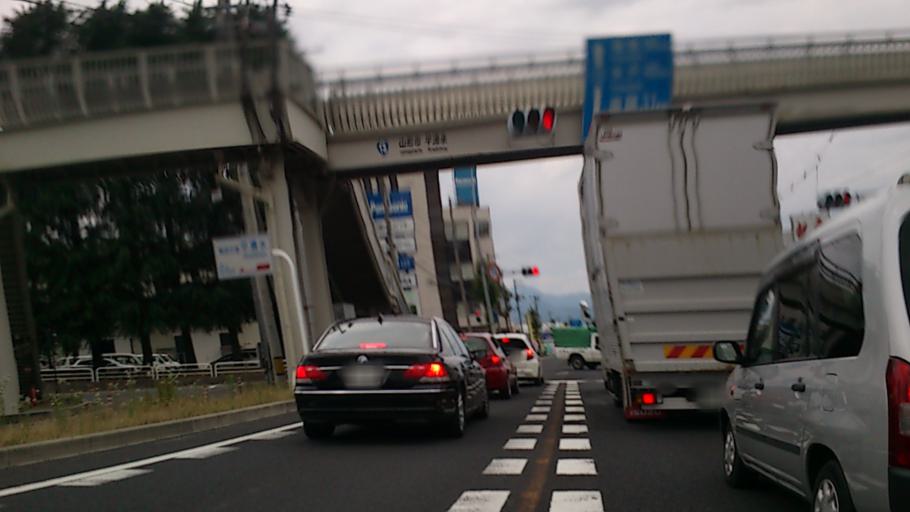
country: JP
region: Yamagata
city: Yamagata-shi
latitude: 38.2330
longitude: 140.3472
